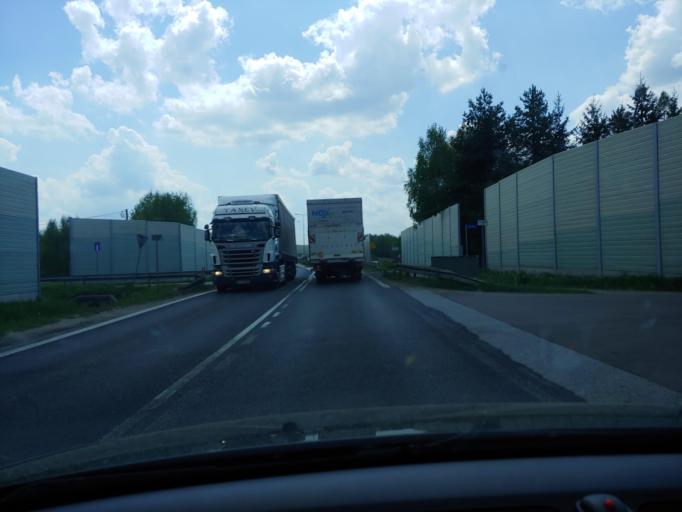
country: PL
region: Lesser Poland Voivodeship
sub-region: Powiat tarnowski
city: Lisia Gora
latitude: 50.0583
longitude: 21.0115
